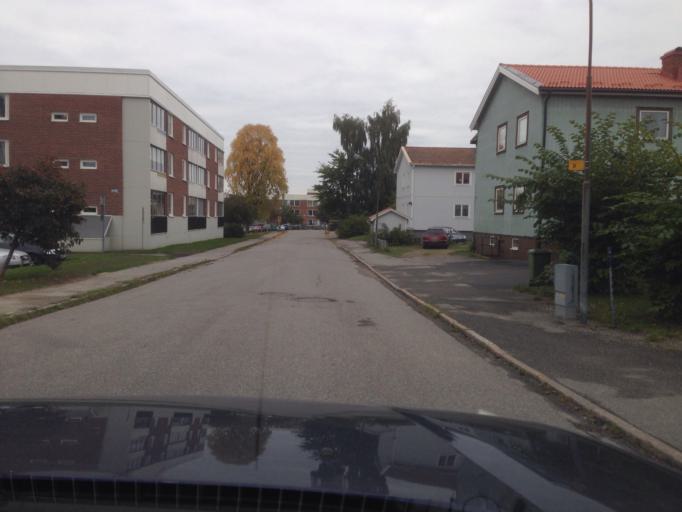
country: SE
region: Vaesternorrland
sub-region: Sundsvalls Kommun
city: Sundsvall
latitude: 62.4003
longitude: 17.3301
